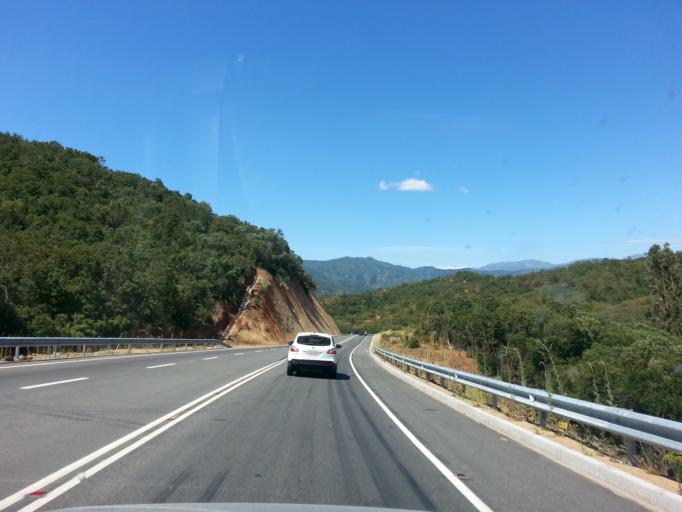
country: CL
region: Valparaiso
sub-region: Provincia de Marga Marga
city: Villa Alemana
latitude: -33.1734
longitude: -71.3560
